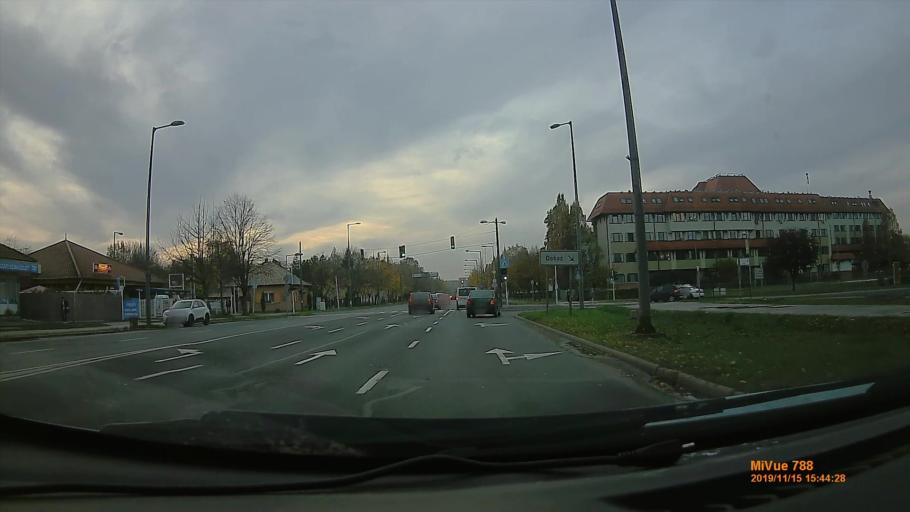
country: HU
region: Bekes
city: Bekescsaba
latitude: 46.6820
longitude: 21.1074
